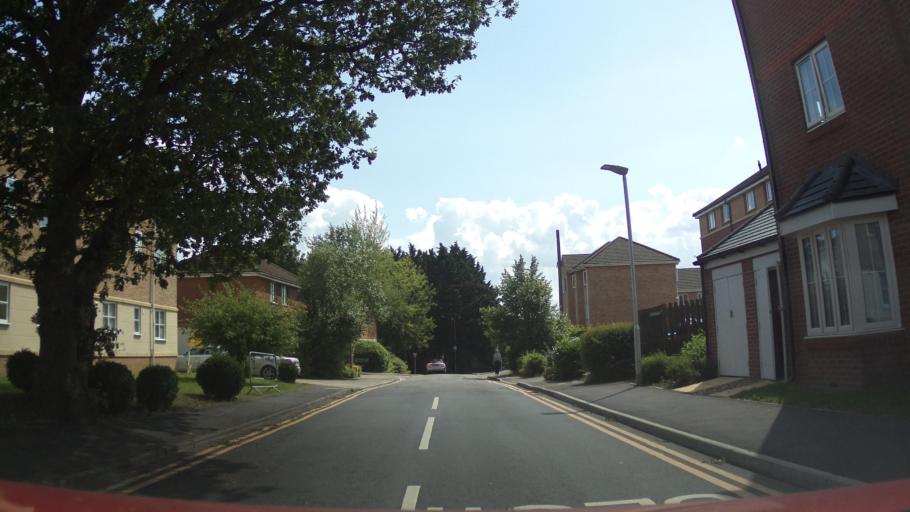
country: GB
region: England
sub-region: West Berkshire
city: Thatcham
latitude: 51.4028
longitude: -1.2811
